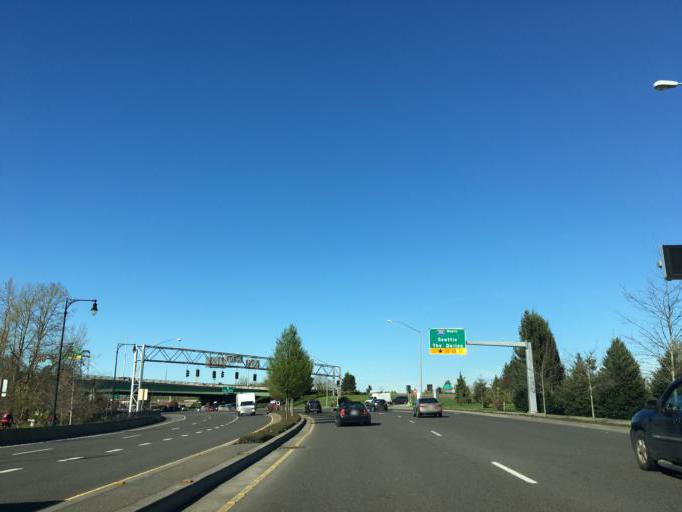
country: US
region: Oregon
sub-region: Clackamas County
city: Oregon City
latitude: 45.3633
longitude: -122.6015
